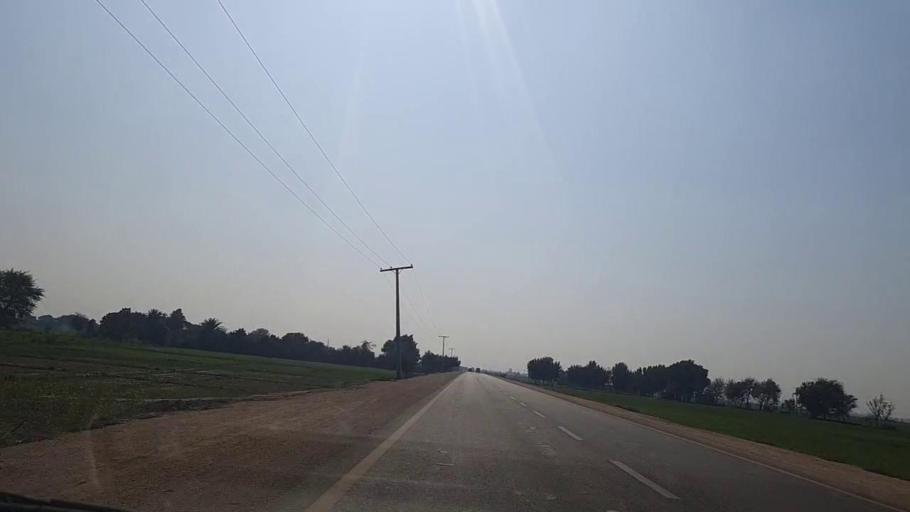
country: PK
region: Sindh
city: Sakrand
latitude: 26.0214
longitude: 68.3974
